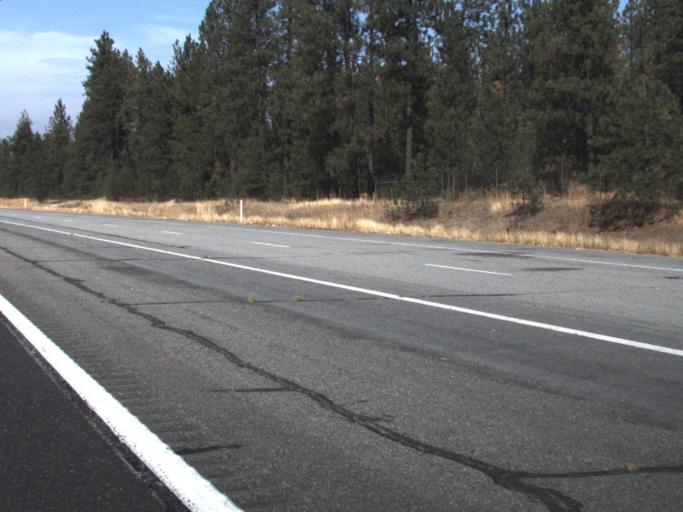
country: US
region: Washington
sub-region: Spokane County
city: Mead
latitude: 47.8635
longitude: -117.3560
